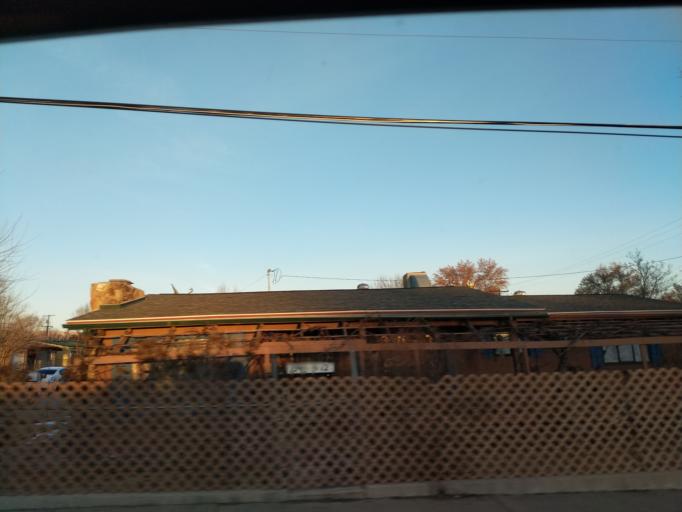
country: US
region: Colorado
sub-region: Mesa County
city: Grand Junction
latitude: 39.0941
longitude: -108.5523
